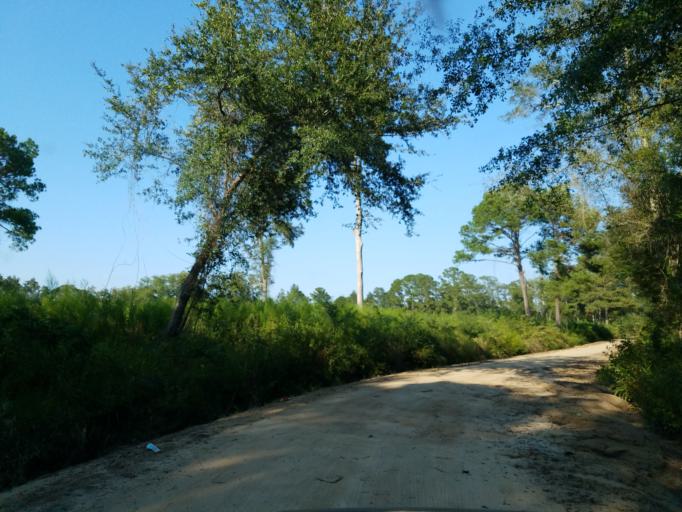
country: US
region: Georgia
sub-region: Lowndes County
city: Hahira
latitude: 31.0393
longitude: -83.3942
